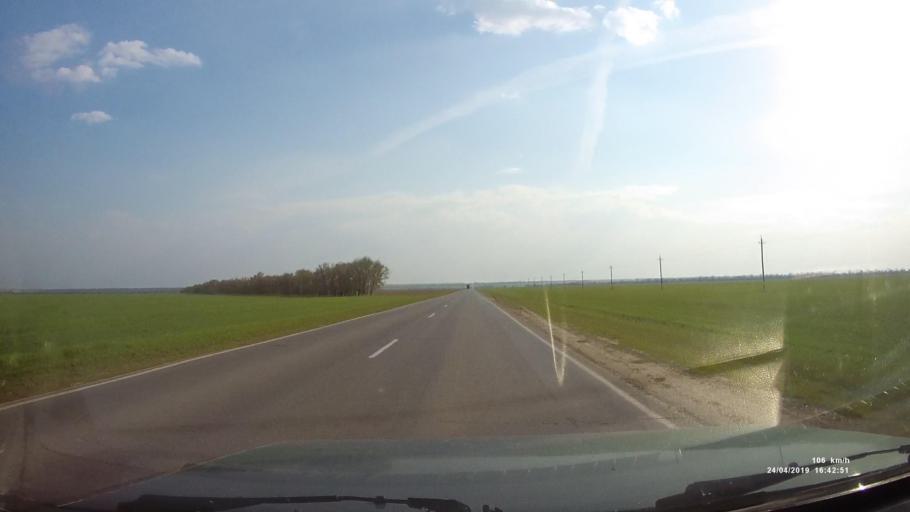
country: RU
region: Rostov
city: Gundorovskiy
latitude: 46.8018
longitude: 41.8481
